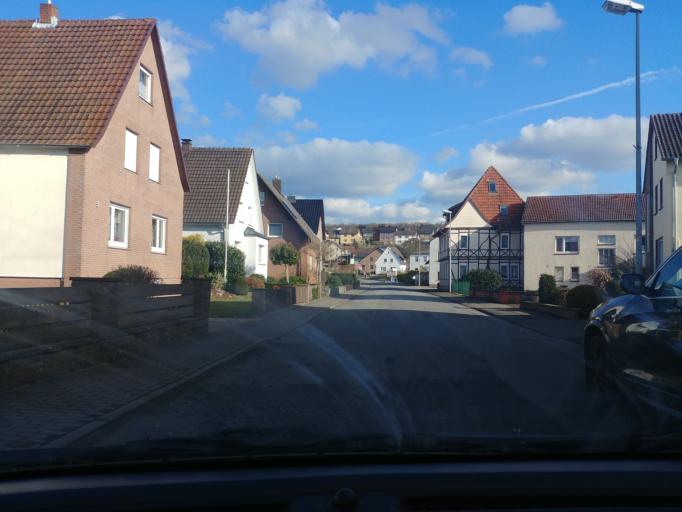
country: DE
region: Lower Saxony
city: Holzminden
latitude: 51.7946
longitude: 9.4284
